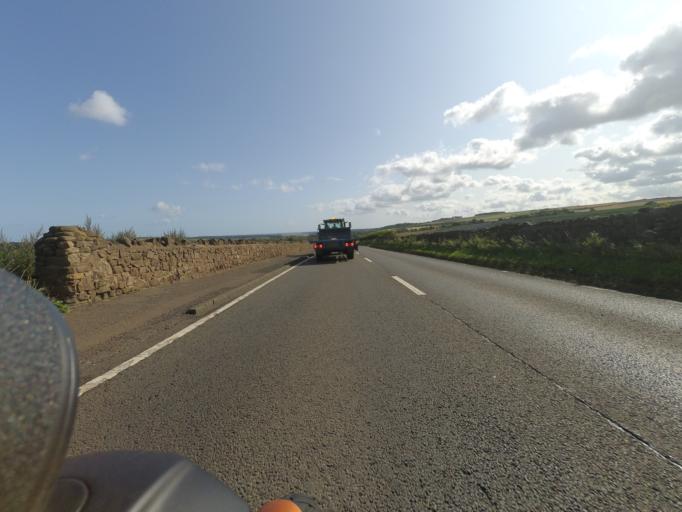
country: GB
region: Scotland
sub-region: East Lothian
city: East Linton
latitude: 55.9820
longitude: -2.6727
